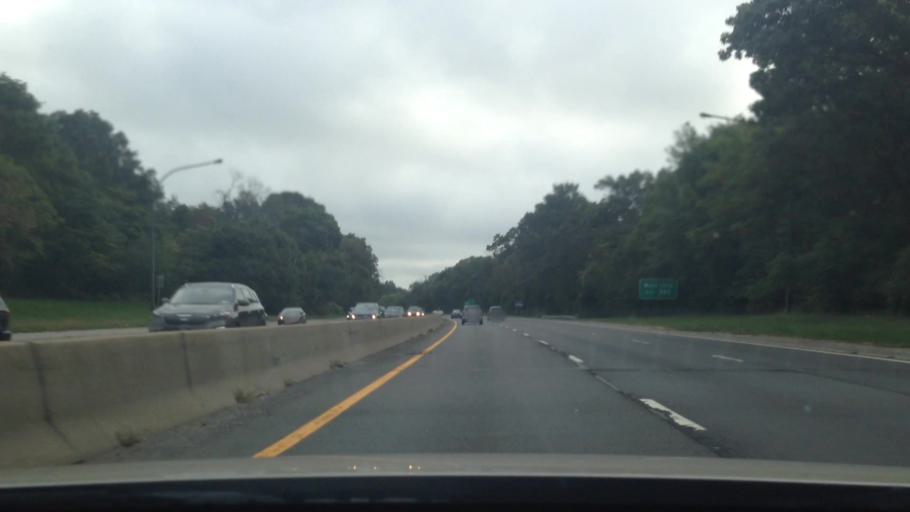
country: US
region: New York
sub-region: Suffolk County
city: North Babylon
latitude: 40.7319
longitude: -73.3297
